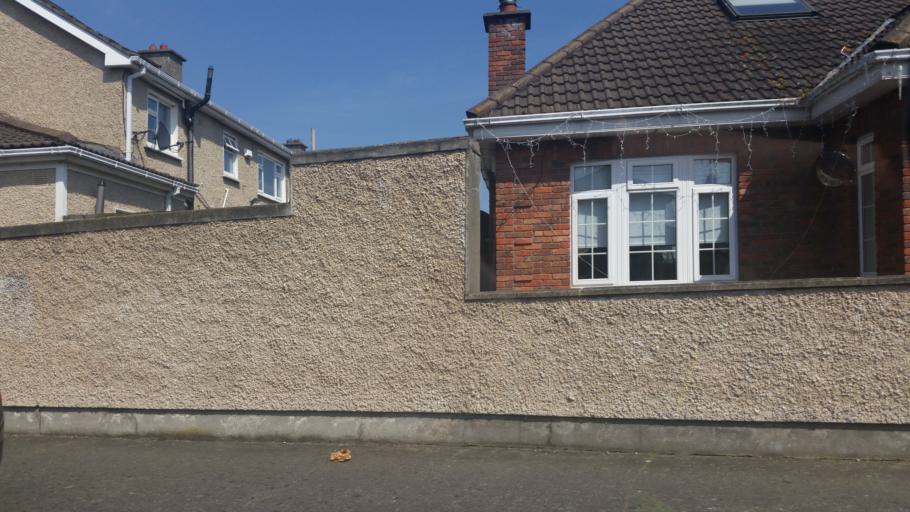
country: IE
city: Bonnybrook
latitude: 53.3997
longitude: -6.2098
